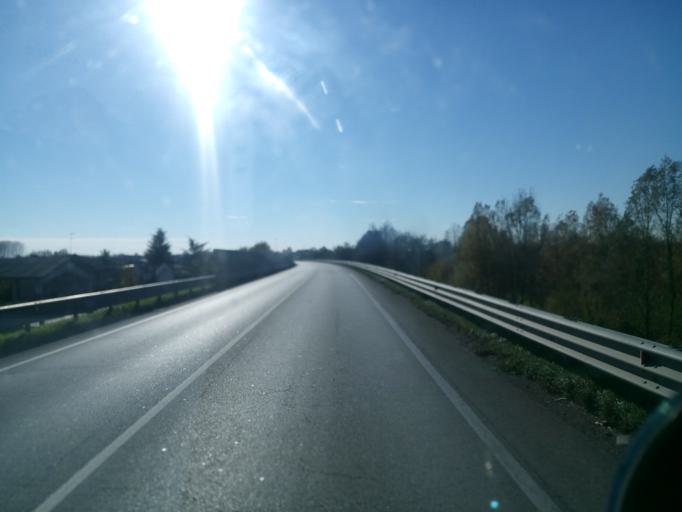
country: IT
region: Veneto
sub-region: Provincia di Padova
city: Loreggia
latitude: 45.5950
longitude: 11.9564
